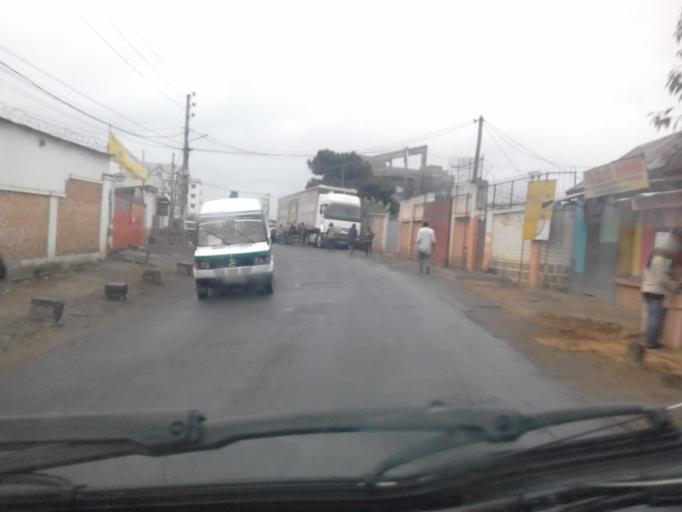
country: MG
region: Analamanga
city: Antananarivo
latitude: -18.8674
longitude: 47.5511
